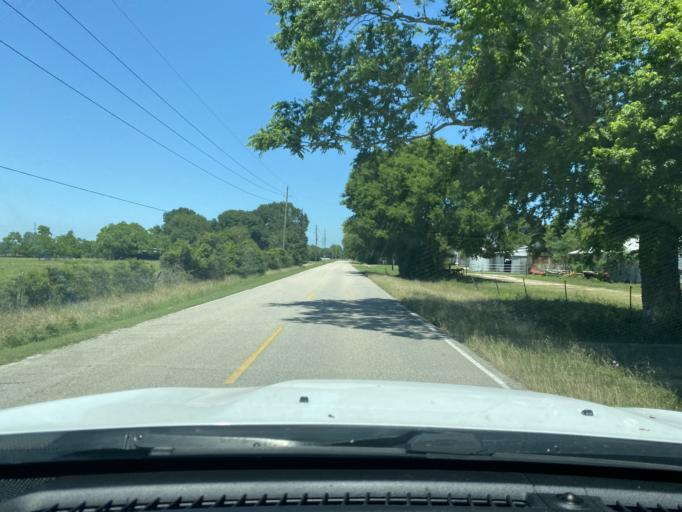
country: US
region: Texas
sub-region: Waller County
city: Waller
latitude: 30.0136
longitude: -95.8486
